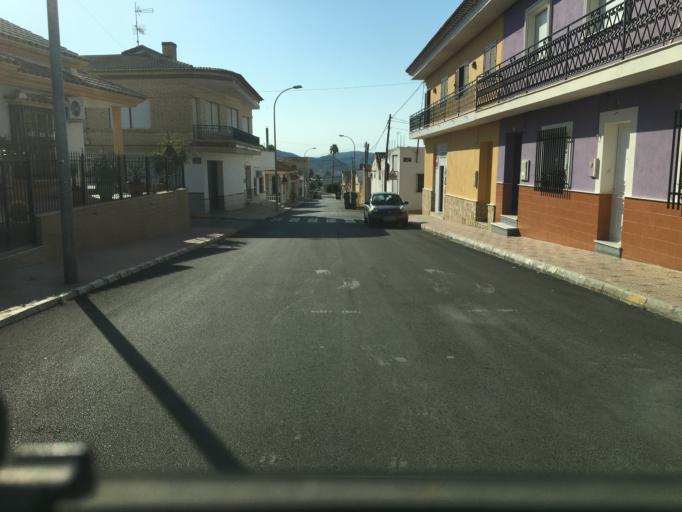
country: ES
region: Murcia
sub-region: Murcia
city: Puerto Lumbreras
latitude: 37.5523
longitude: -1.8161
